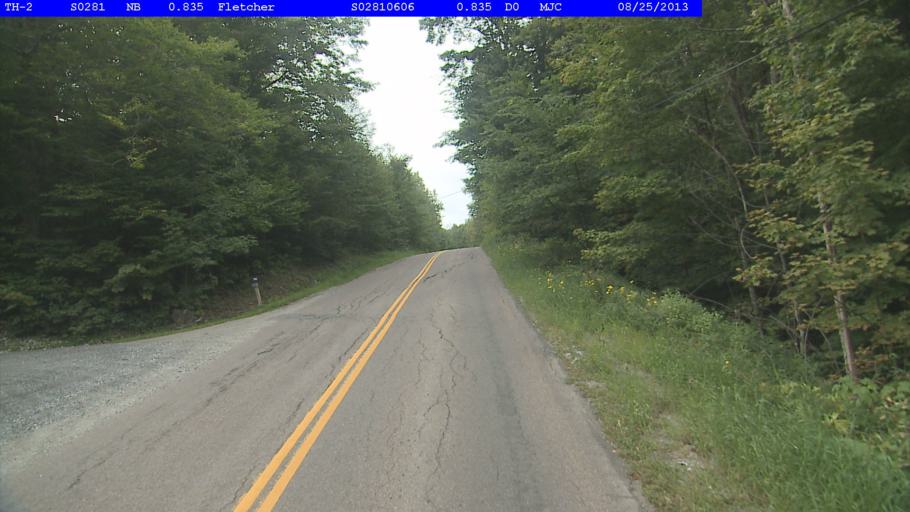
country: US
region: Vermont
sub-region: Chittenden County
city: Milton
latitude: 44.6908
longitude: -72.9263
